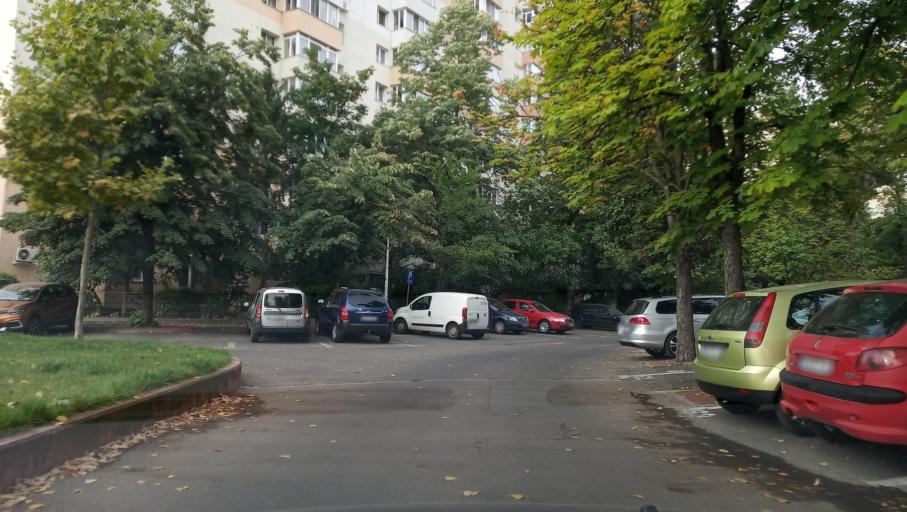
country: RO
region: Ilfov
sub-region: Comuna Popesti-Leordeni
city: Popesti-Leordeni
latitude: 44.4170
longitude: 26.1600
